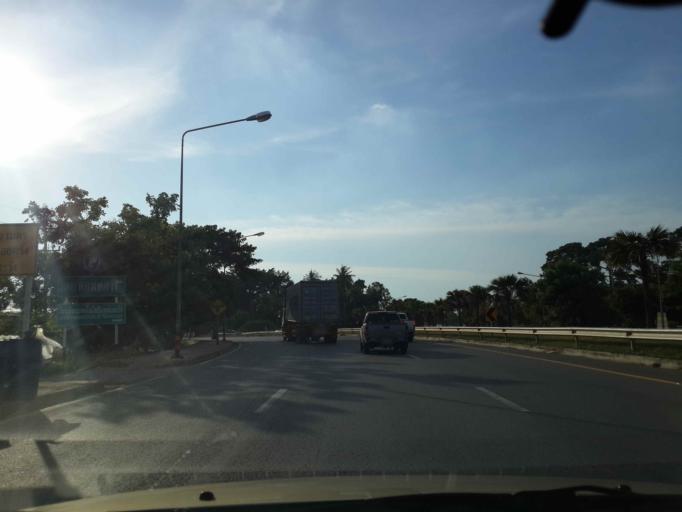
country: TH
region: Chon Buri
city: Bang Lamung
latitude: 13.0006
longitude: 100.9321
